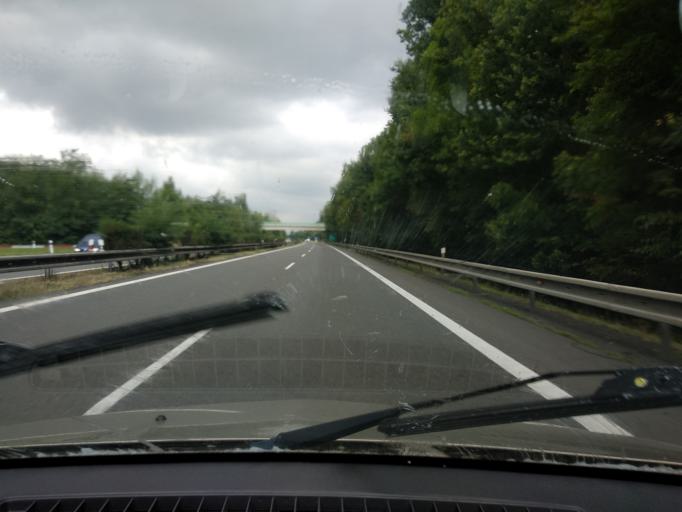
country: CZ
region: Olomoucky
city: Bila Lhota
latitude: 49.7094
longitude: 17.0238
